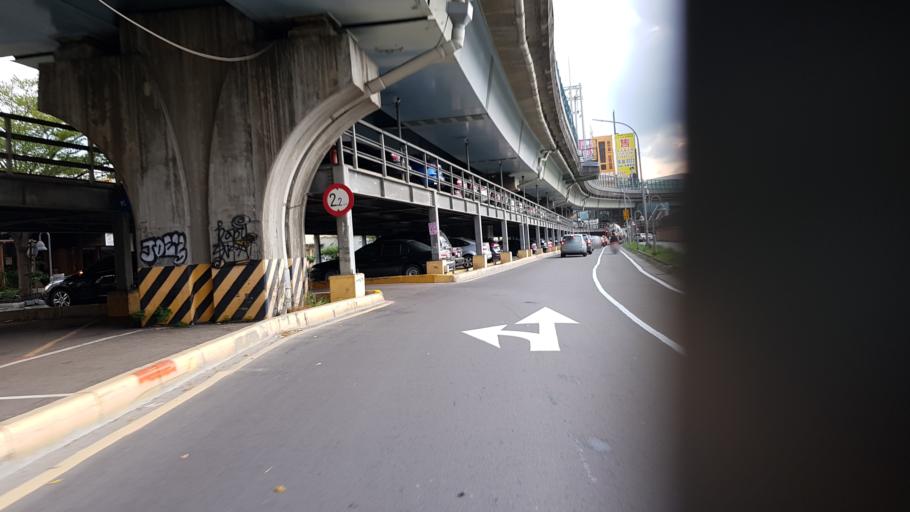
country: TW
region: Taiwan
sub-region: Hsinchu
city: Hsinchu
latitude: 24.7886
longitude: 121.0108
